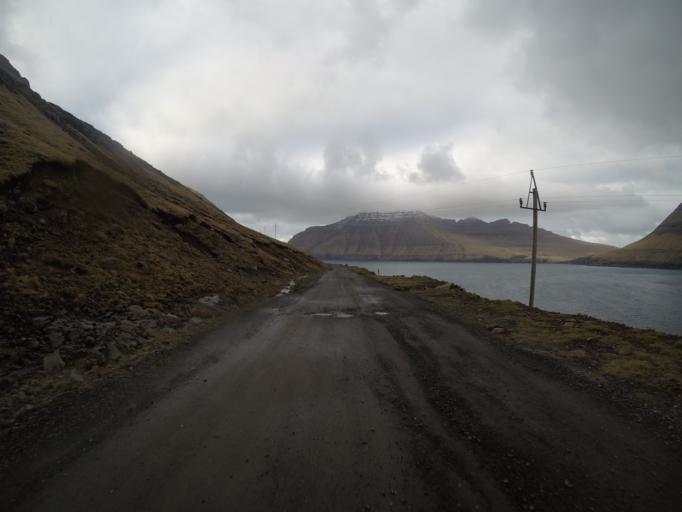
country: FO
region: Nordoyar
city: Klaksvik
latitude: 62.3430
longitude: -6.5803
